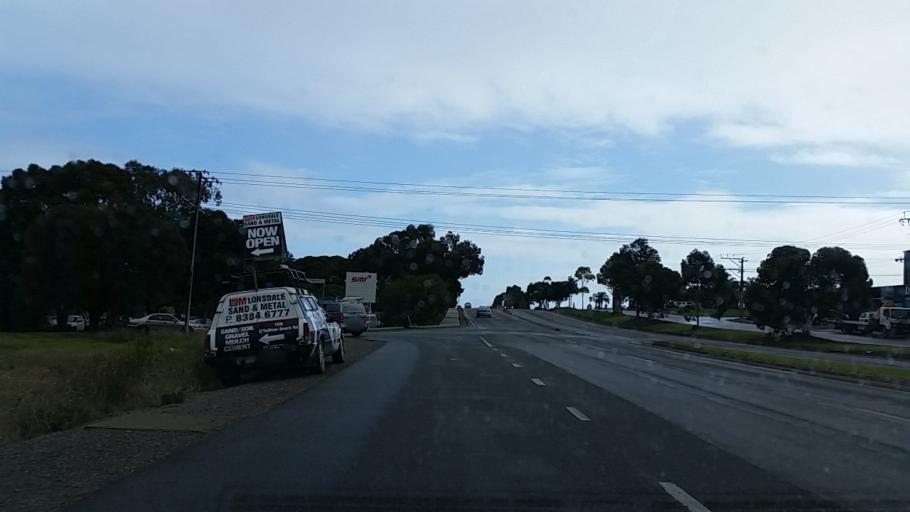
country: AU
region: South Australia
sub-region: Onkaparinga
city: Reynella
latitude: -35.1061
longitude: 138.5075
